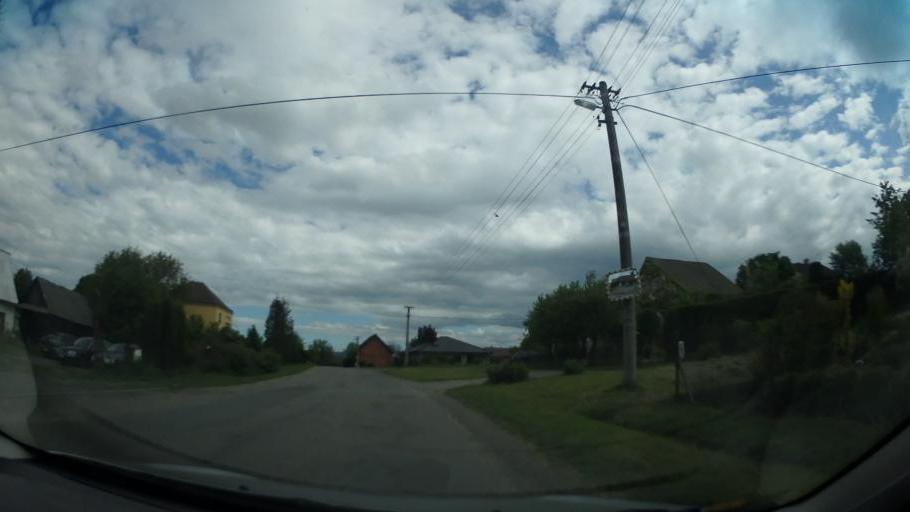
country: CZ
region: Pardubicky
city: Kuncina
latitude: 49.8400
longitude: 16.6981
